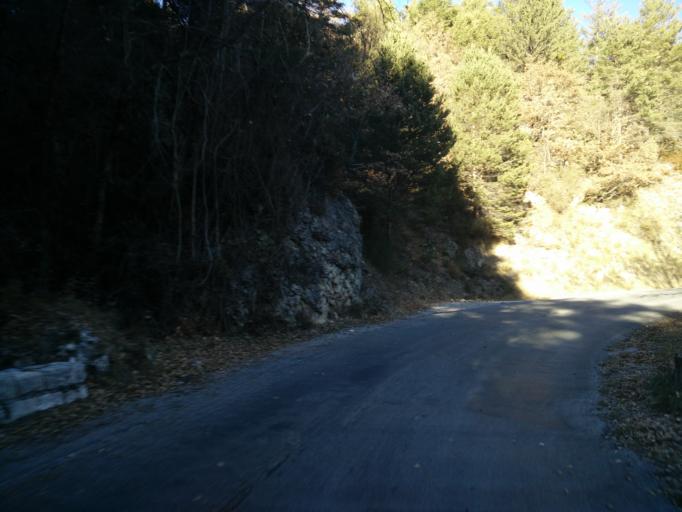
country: FR
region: Provence-Alpes-Cote d'Azur
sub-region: Departement des Alpes-de-Haute-Provence
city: Castellane
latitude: 43.7930
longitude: 6.4012
